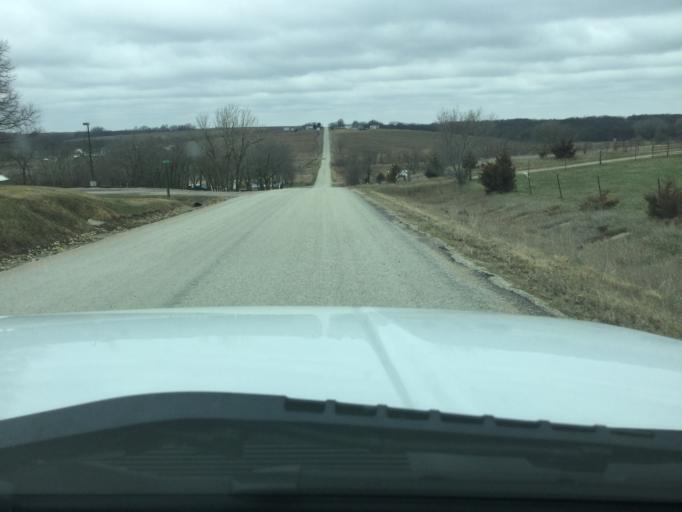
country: US
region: Kansas
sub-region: Nemaha County
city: Seneca
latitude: 39.7399
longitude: -96.0013
